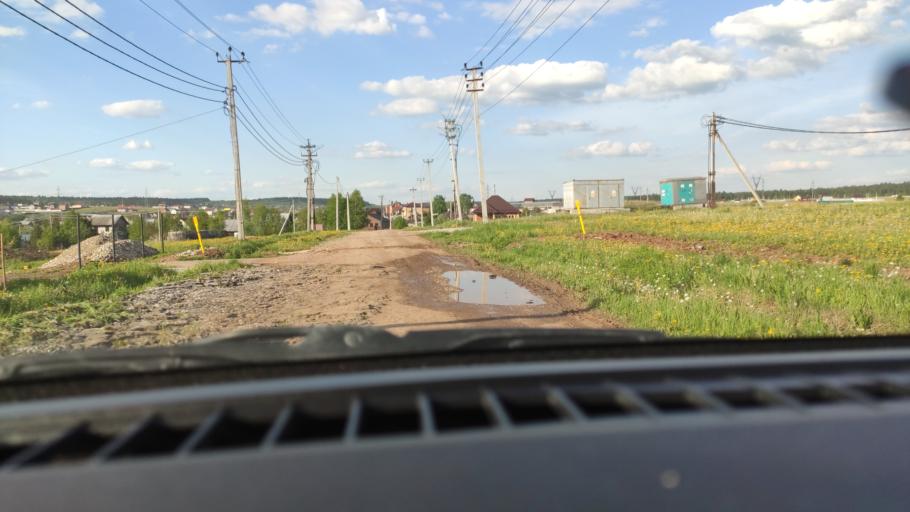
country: RU
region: Perm
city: Ferma
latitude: 57.9382
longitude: 56.3550
